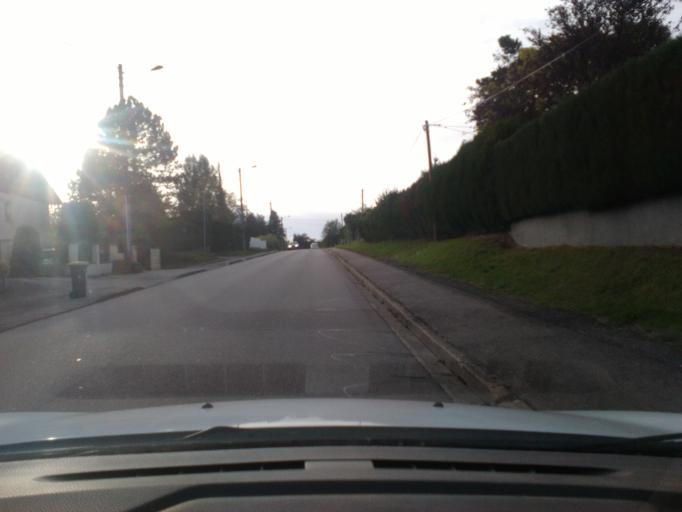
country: FR
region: Lorraine
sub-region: Departement des Vosges
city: Chantraine
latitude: 48.1767
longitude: 6.4224
